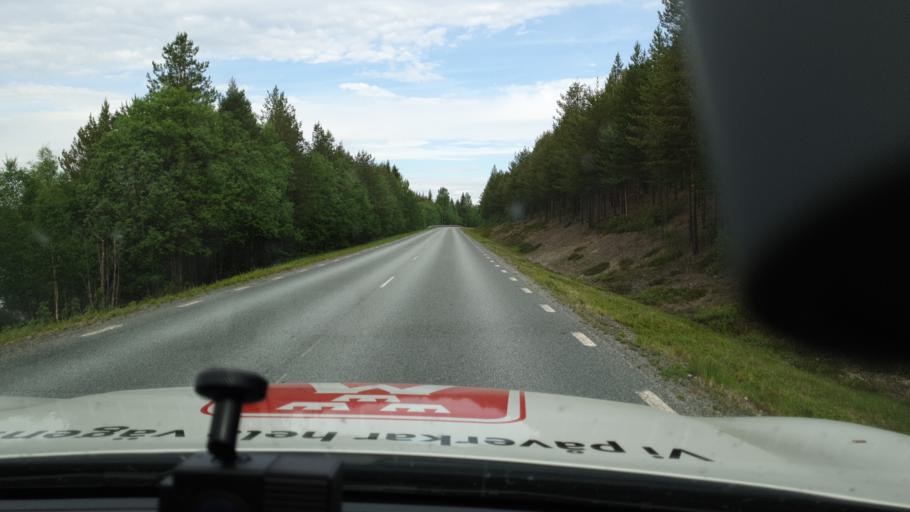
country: SE
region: Vaesterbotten
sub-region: Mala Kommun
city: Mala
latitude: 65.0163
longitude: 18.4446
